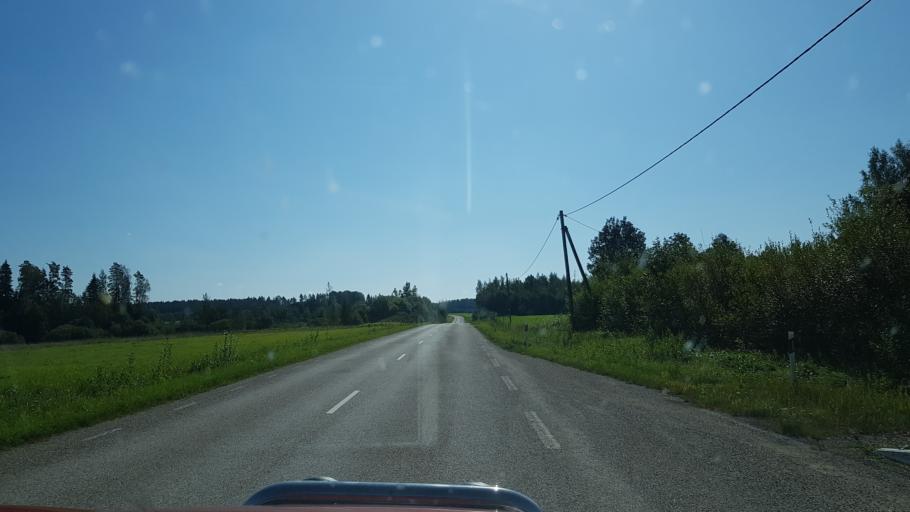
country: EE
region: Polvamaa
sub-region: Polva linn
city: Polva
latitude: 58.2276
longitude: 27.2260
